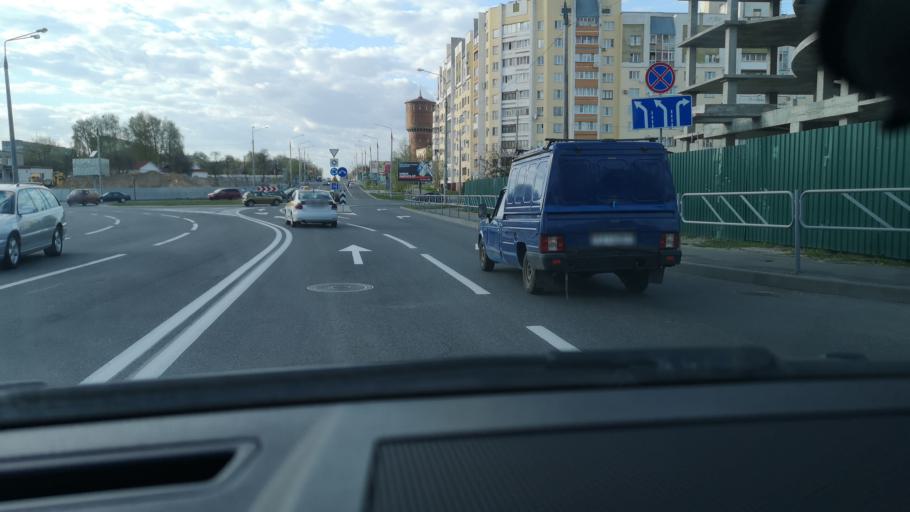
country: BY
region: Gomel
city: Gomel
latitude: 52.4390
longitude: 30.9997
